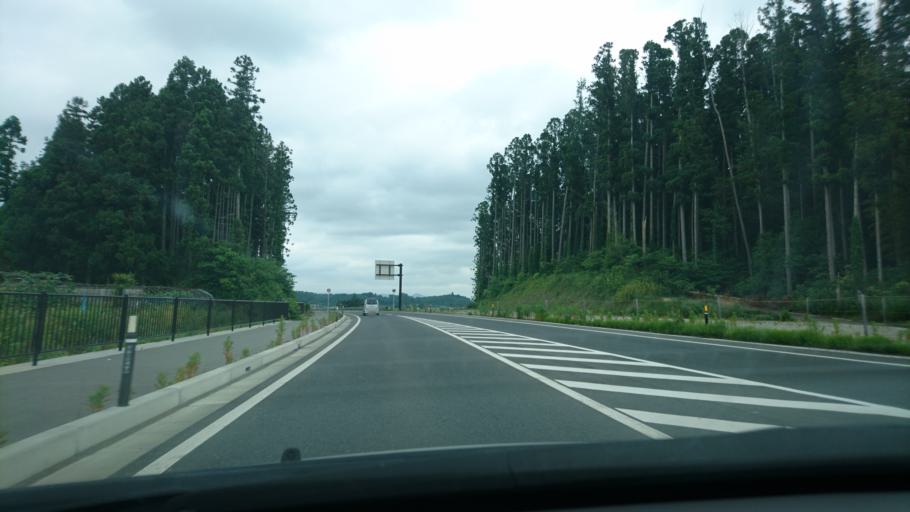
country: JP
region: Miyagi
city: Furukawa
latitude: 38.7431
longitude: 141.0388
